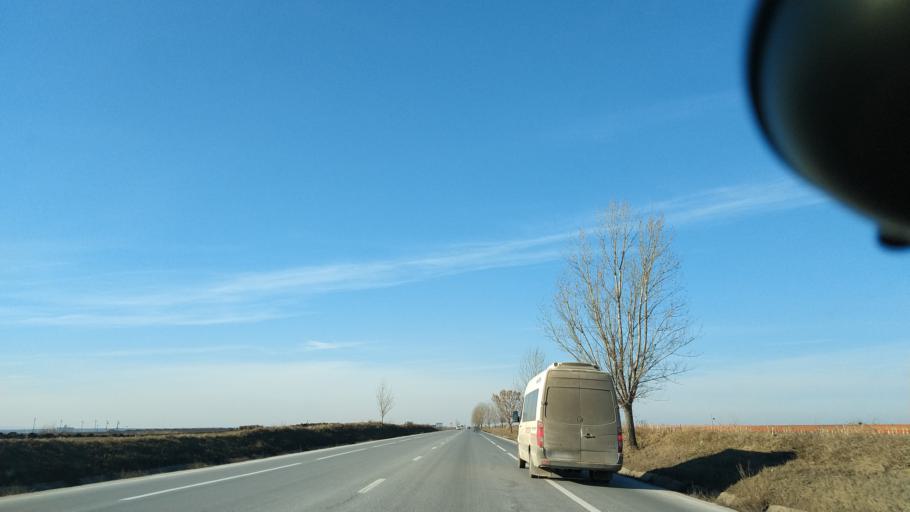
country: RO
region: Iasi
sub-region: Comuna Podu Iloaiei
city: Budai
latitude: 47.2199
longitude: 27.2045
